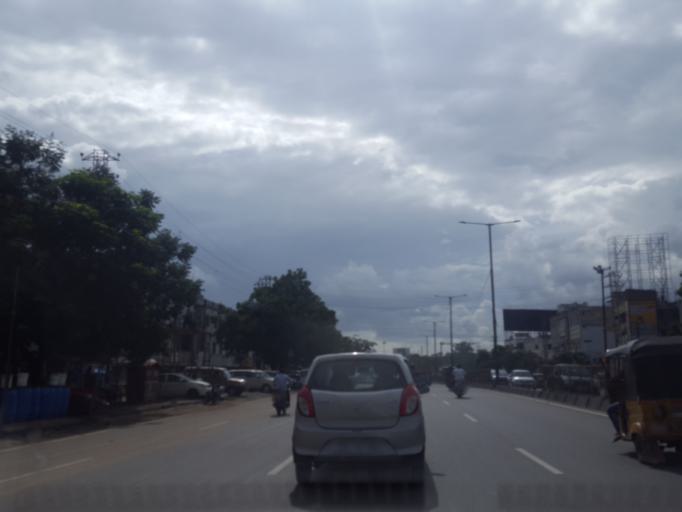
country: IN
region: Telangana
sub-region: Medak
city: Serilingampalle
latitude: 17.4950
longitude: 78.3201
